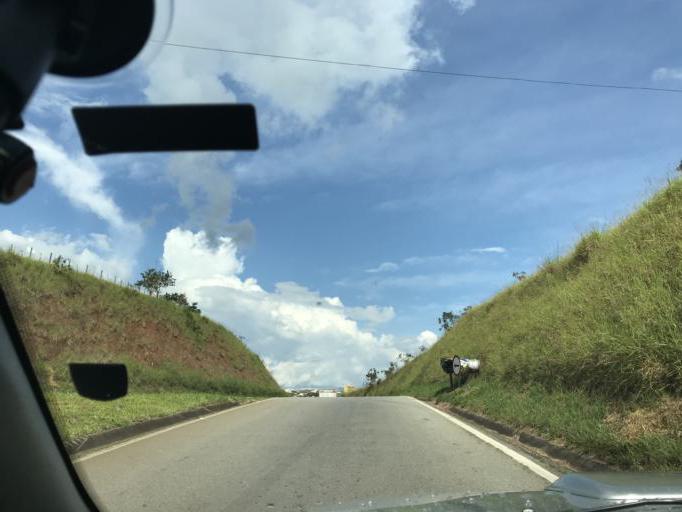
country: BR
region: Minas Gerais
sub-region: Tres Coracoes
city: Tres Coracoes
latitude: -21.6578
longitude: -45.2999
